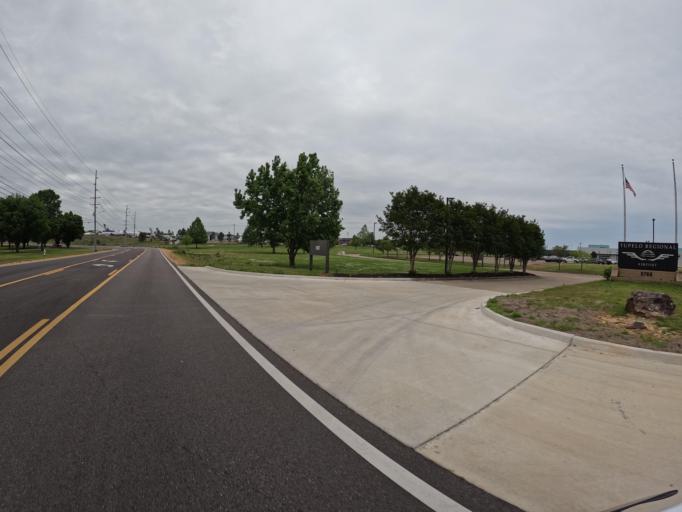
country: US
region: Mississippi
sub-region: Lee County
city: Tupelo
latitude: 34.2663
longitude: -88.7642
